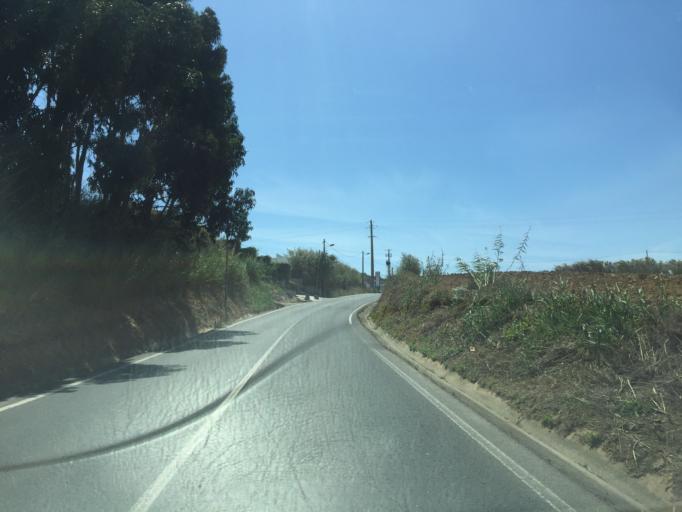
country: PT
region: Lisbon
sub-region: Lourinha
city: Lourinha
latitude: 39.2307
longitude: -9.3123
